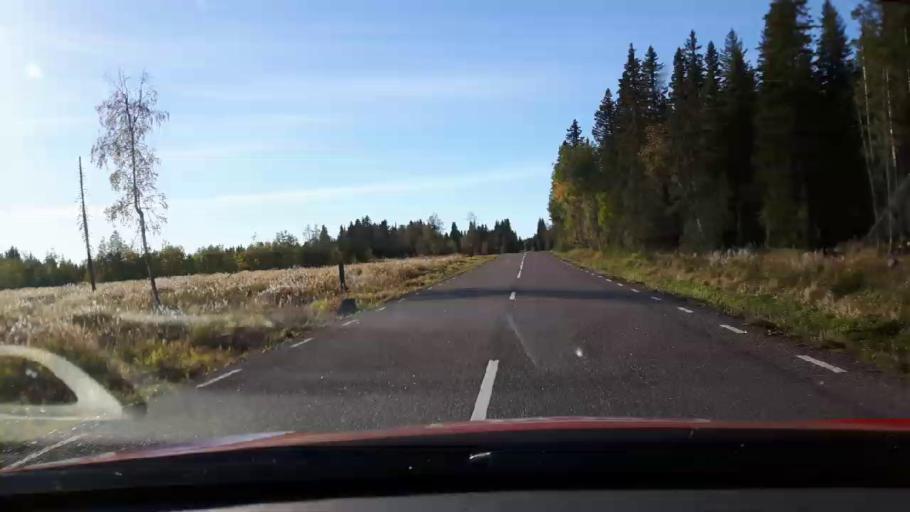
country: SE
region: Jaemtland
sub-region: Stroemsunds Kommun
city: Stroemsund
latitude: 63.8634
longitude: 15.1572
